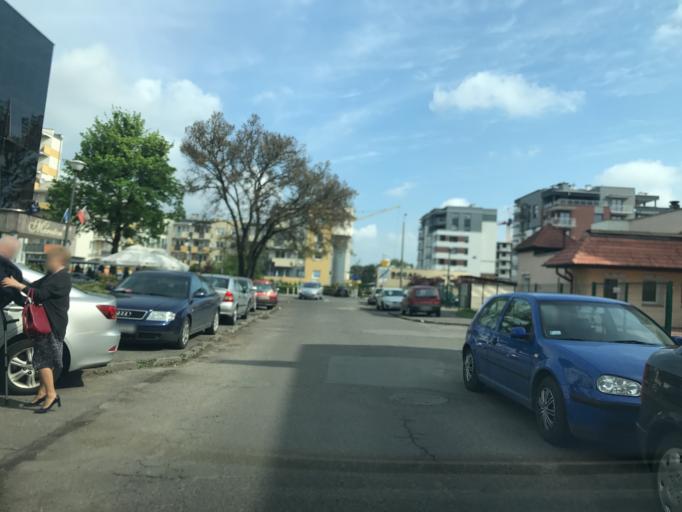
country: PL
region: Kujawsko-Pomorskie
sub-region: Bydgoszcz
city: Bydgoszcz
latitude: 53.1432
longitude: 18.0087
